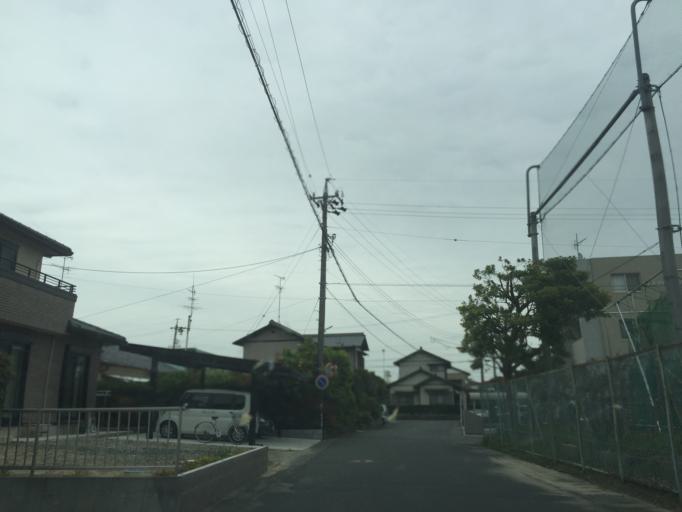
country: JP
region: Shizuoka
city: Kakegawa
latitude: 34.7747
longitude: 138.0007
